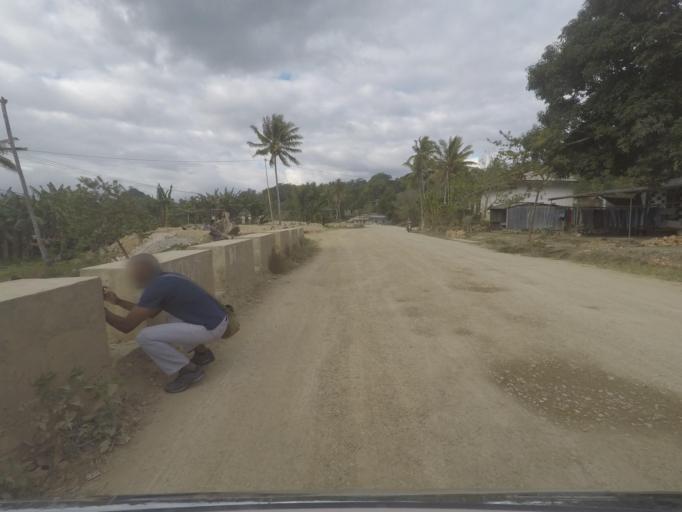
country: TL
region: Baucau
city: Venilale
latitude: -8.5935
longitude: 126.3853
